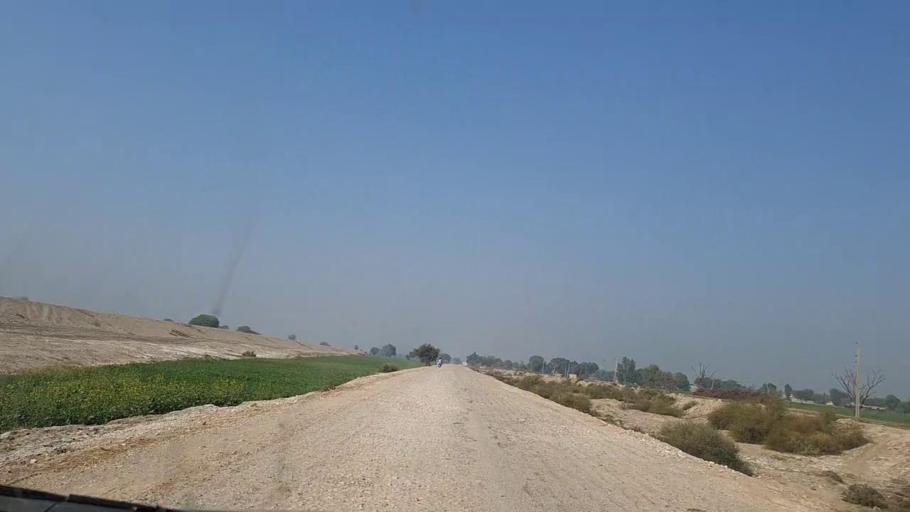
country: PK
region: Sindh
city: Moro
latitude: 26.7267
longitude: 67.9215
